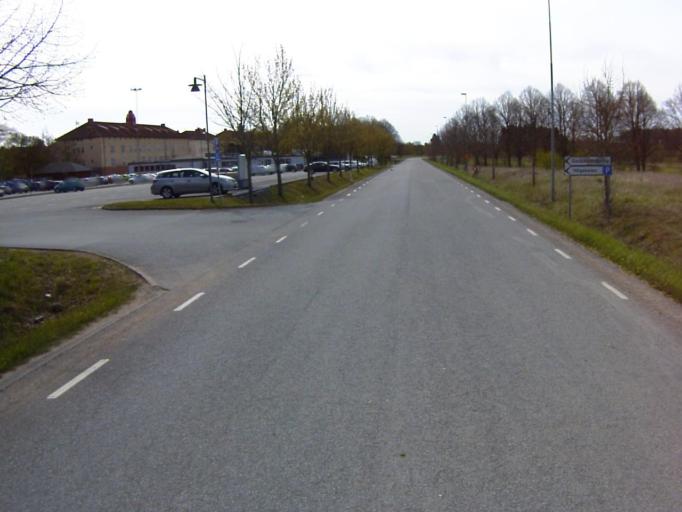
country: SE
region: Skane
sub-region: Kristianstads Kommun
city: Kristianstad
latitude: 56.0500
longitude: 14.1433
